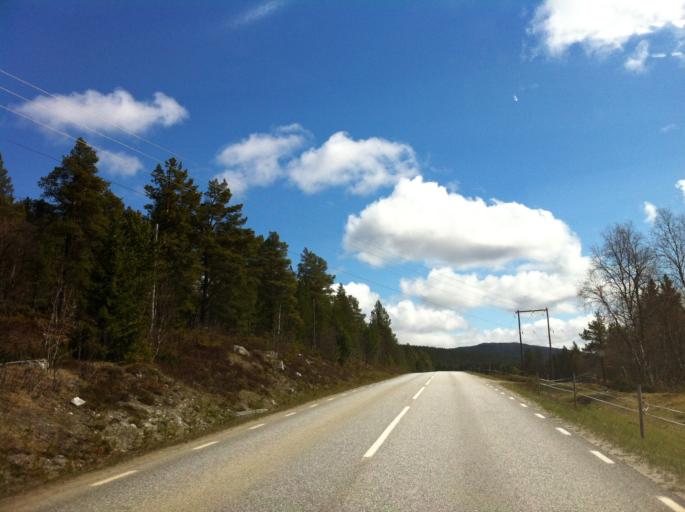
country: NO
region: Sor-Trondelag
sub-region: Tydal
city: Aas
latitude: 62.6179
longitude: 12.4807
